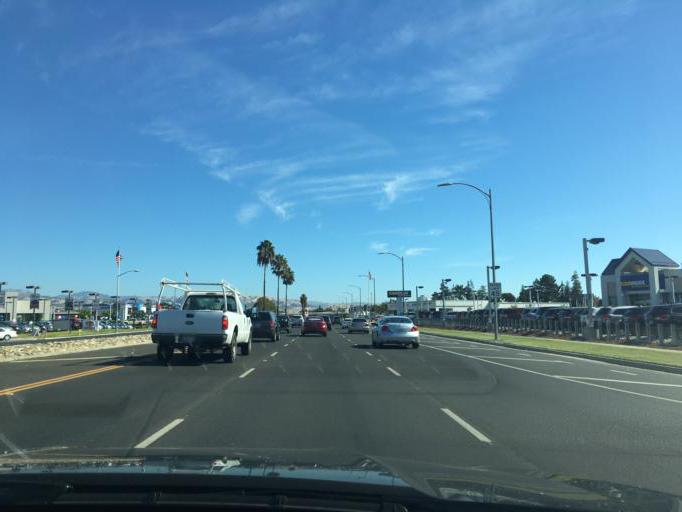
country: US
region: California
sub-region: Santa Clara County
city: Seven Trees
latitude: 37.2751
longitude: -121.8699
